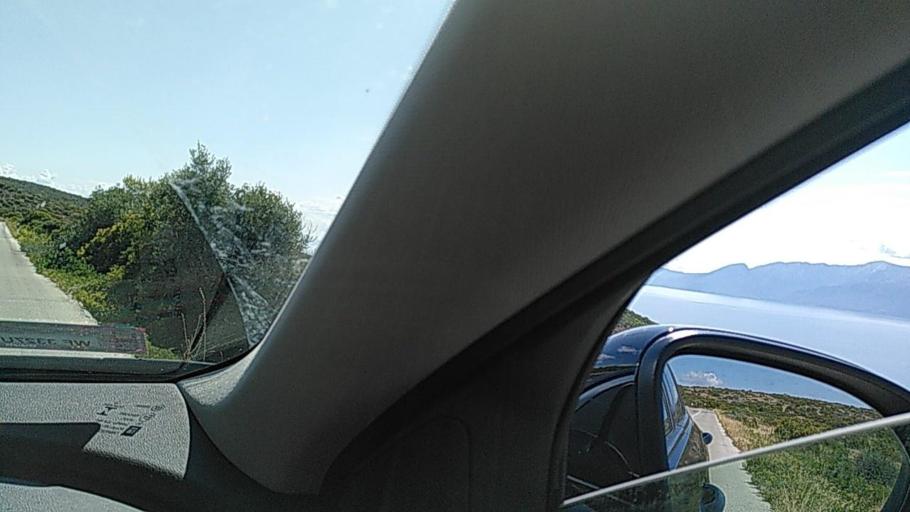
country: HR
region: Splitsko-Dalmatinska
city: Tucepi
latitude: 43.1263
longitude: 17.0930
